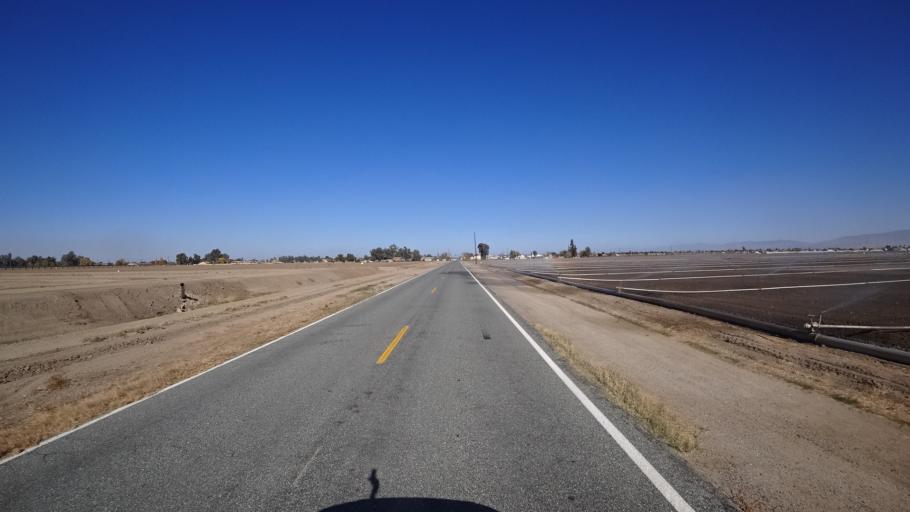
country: US
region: California
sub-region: Kern County
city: Greenfield
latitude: 35.2628
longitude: -119.0567
